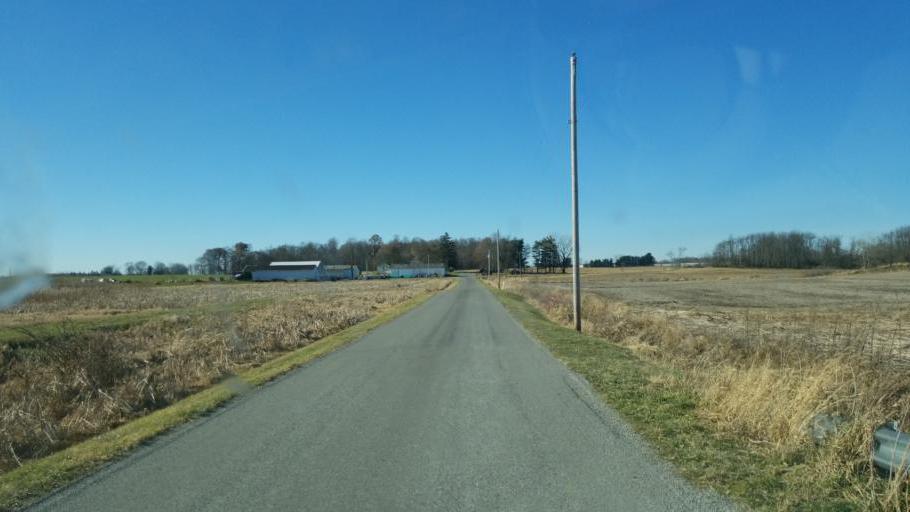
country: US
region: Ohio
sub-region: Richland County
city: Shelby
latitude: 40.9381
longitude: -82.6071
